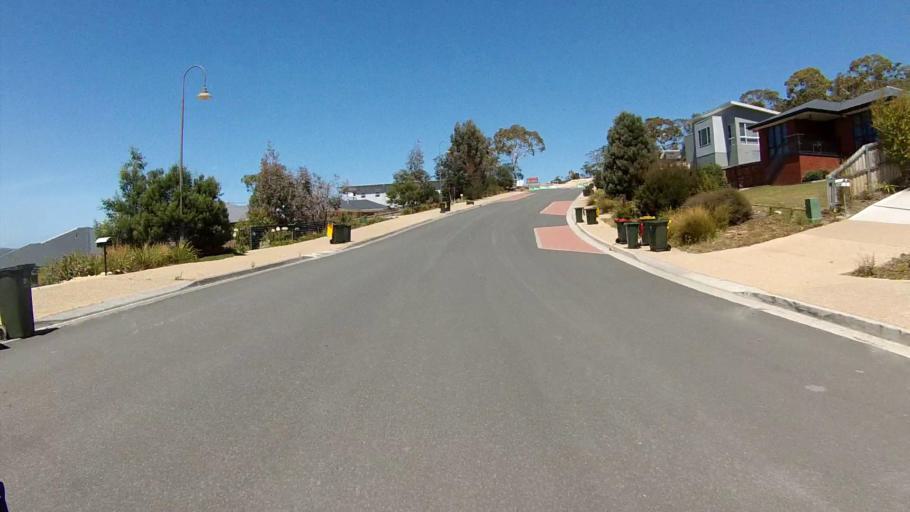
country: AU
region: Tasmania
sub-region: Clarence
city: Rokeby
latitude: -42.9073
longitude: 147.4289
